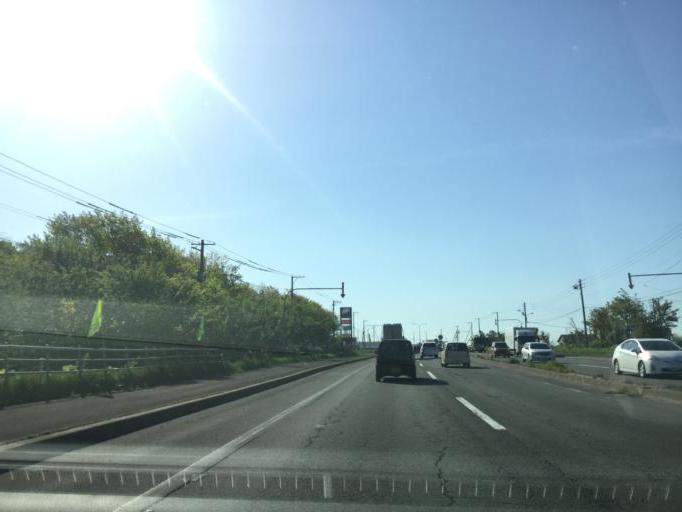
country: JP
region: Hokkaido
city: Kitahiroshima
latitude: 43.0080
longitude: 141.5206
